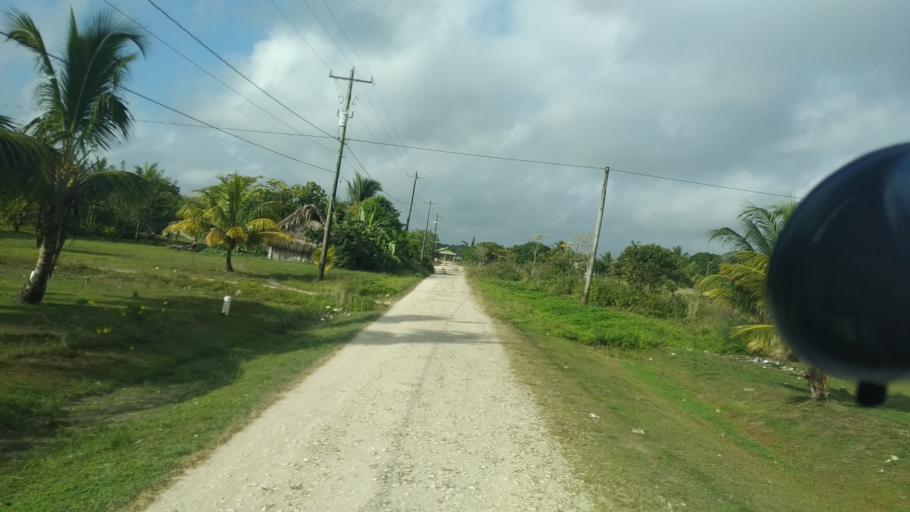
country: BZ
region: Stann Creek
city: Placencia
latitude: 16.5077
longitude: -88.5460
